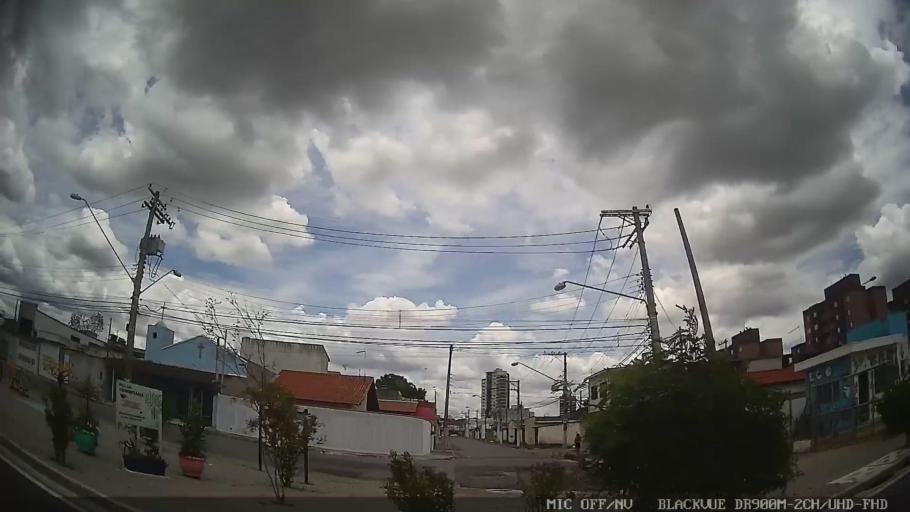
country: BR
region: Sao Paulo
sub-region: Suzano
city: Suzano
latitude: -23.5486
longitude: -46.3043
